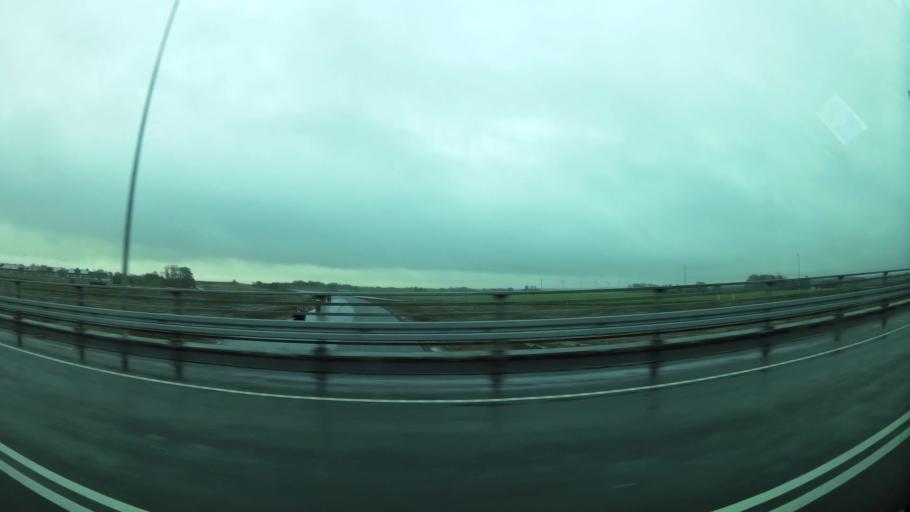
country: DK
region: Central Jutland
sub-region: Herning Kommune
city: Snejbjerg
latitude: 56.1286
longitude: 8.8759
